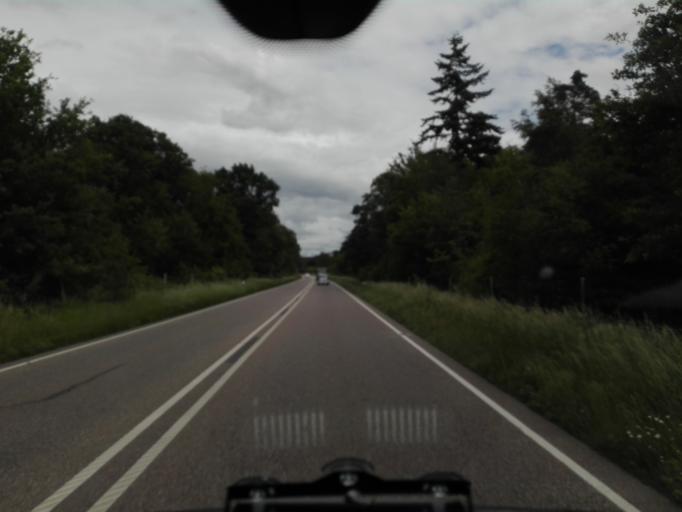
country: DE
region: Baden-Wuerttemberg
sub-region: Karlsruhe Region
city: Linkenheim-Hochstetten
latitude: 49.1062
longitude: 8.4227
